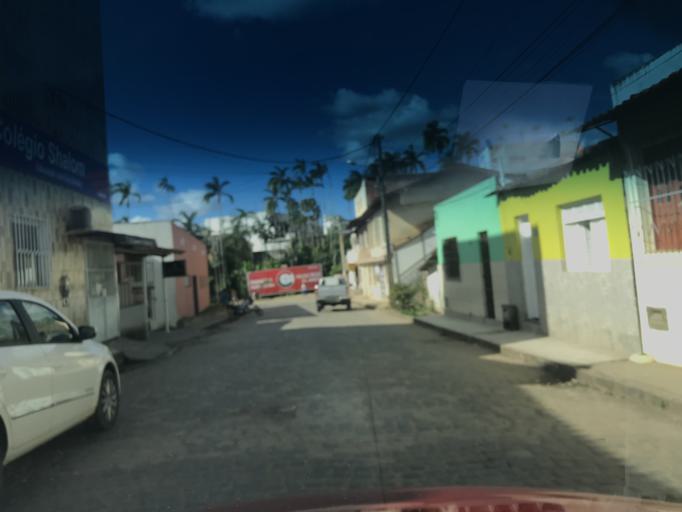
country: BR
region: Bahia
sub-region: Gandu
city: Gandu
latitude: -13.7464
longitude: -39.4890
